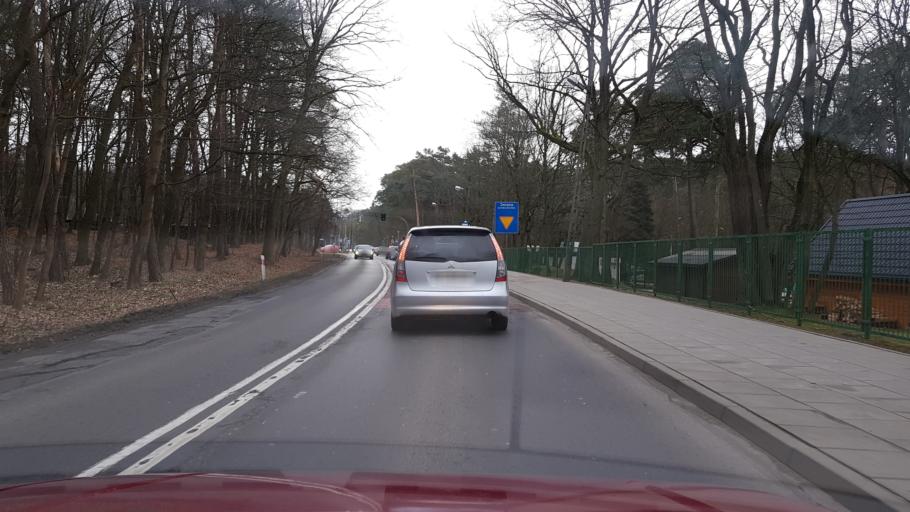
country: PL
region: West Pomeranian Voivodeship
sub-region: Szczecin
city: Szczecin
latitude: 53.4727
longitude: 14.4856
